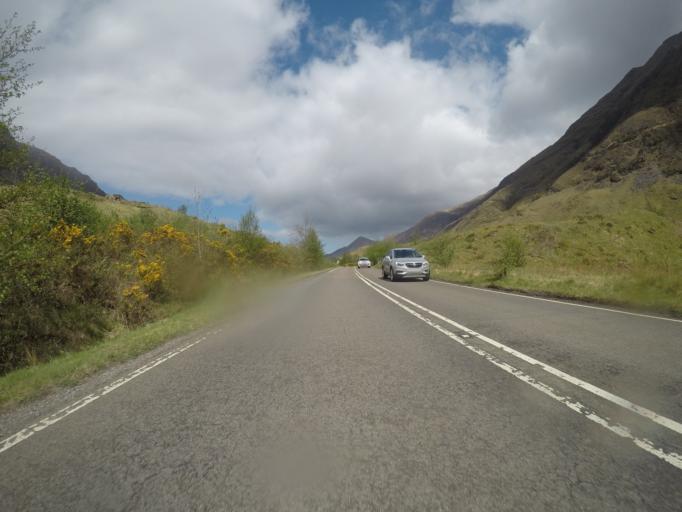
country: GB
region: Scotland
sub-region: Highland
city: Fort William
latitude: 57.1778
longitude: -5.3698
